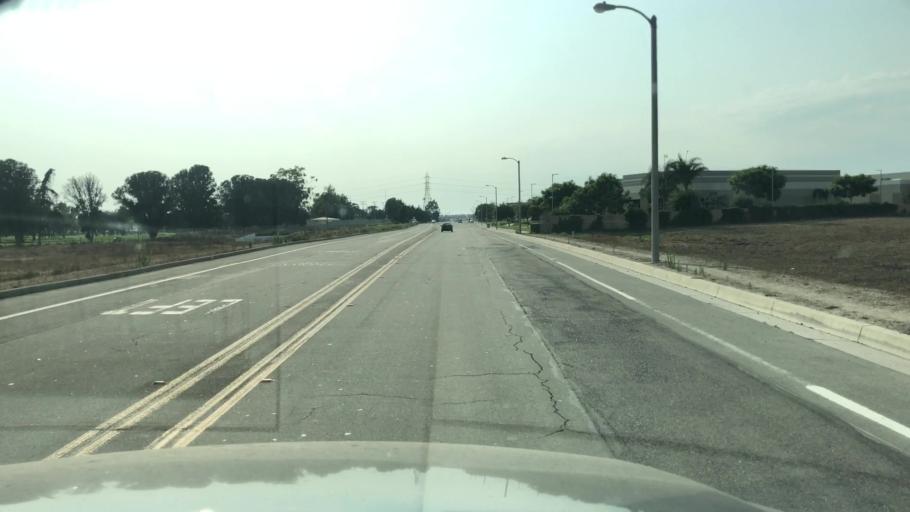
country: US
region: California
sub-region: Ventura County
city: El Rio
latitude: 34.2414
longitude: -119.2041
